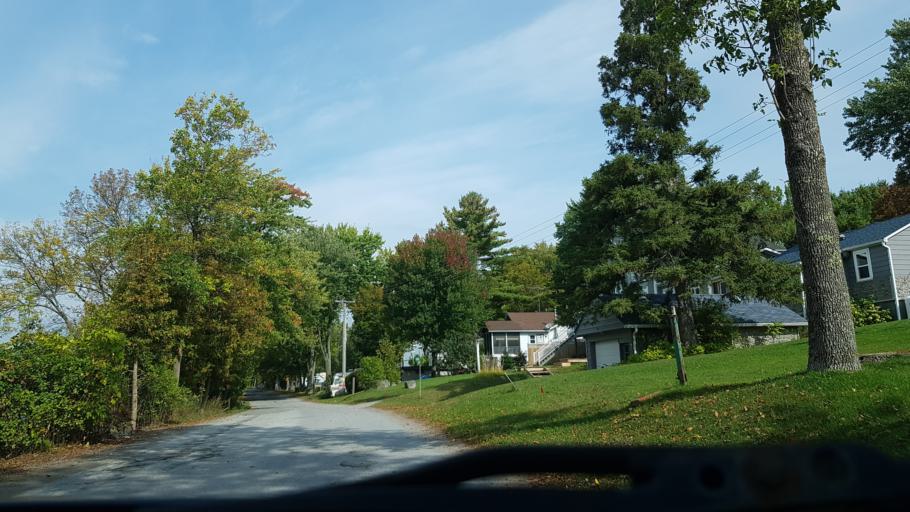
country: CA
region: Ontario
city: Orillia
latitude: 44.6548
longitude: -79.1022
